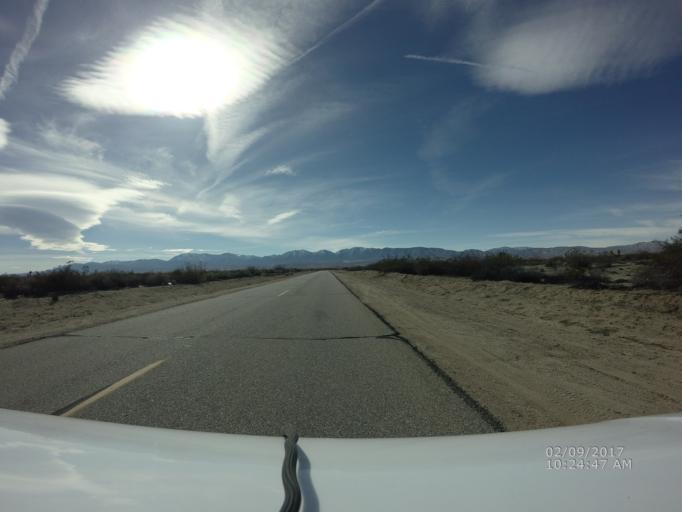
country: US
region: California
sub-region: Los Angeles County
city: Lake Los Angeles
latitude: 34.5605
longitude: -117.8896
